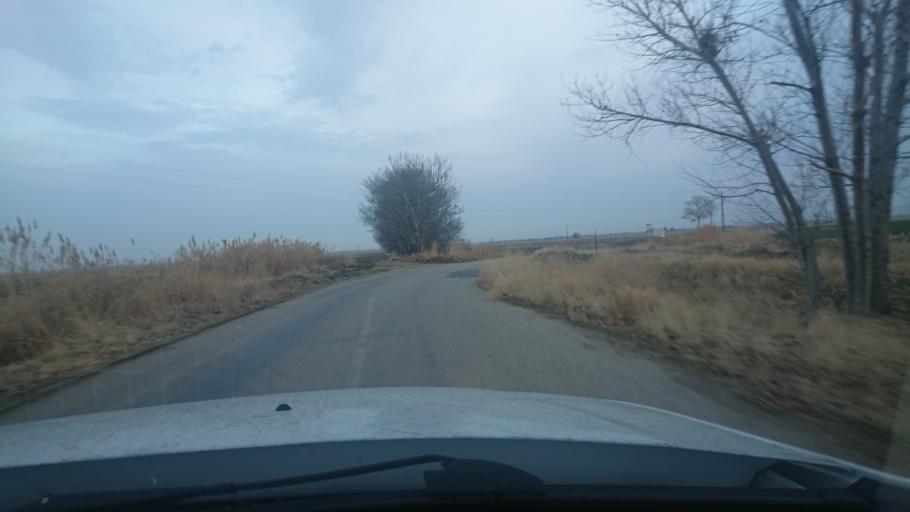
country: TR
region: Aksaray
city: Yesilova
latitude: 38.4473
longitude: 33.8354
